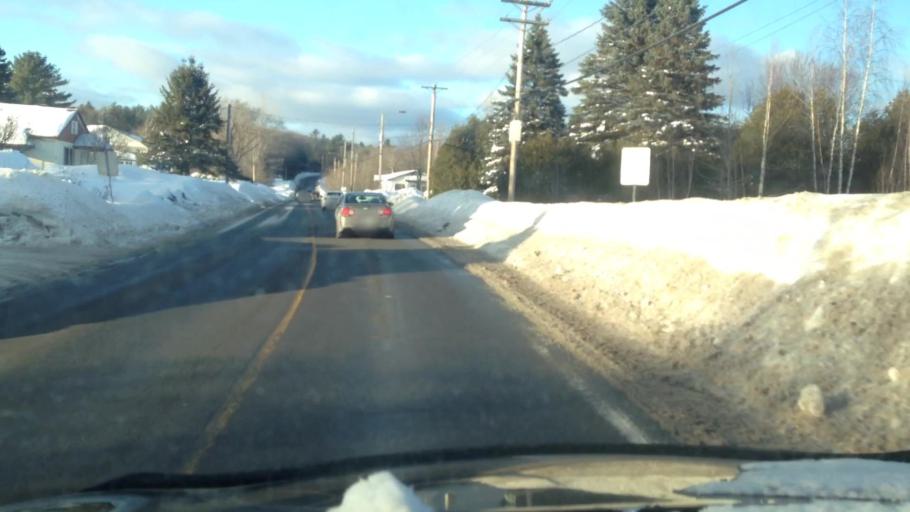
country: CA
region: Quebec
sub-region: Laurentides
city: Saint-Jerome
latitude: 45.8012
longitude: -73.9844
